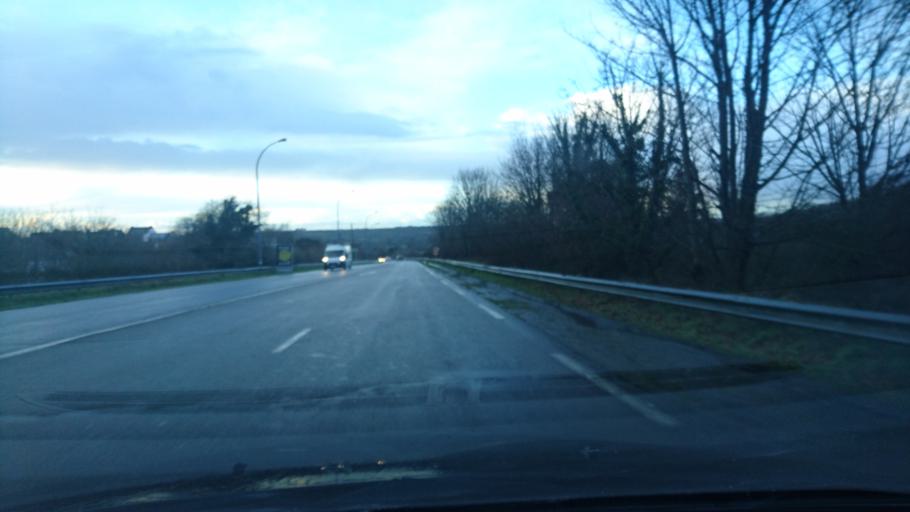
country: FR
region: Brittany
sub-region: Departement du Finistere
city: Bohars
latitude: 48.3880
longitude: -4.5308
